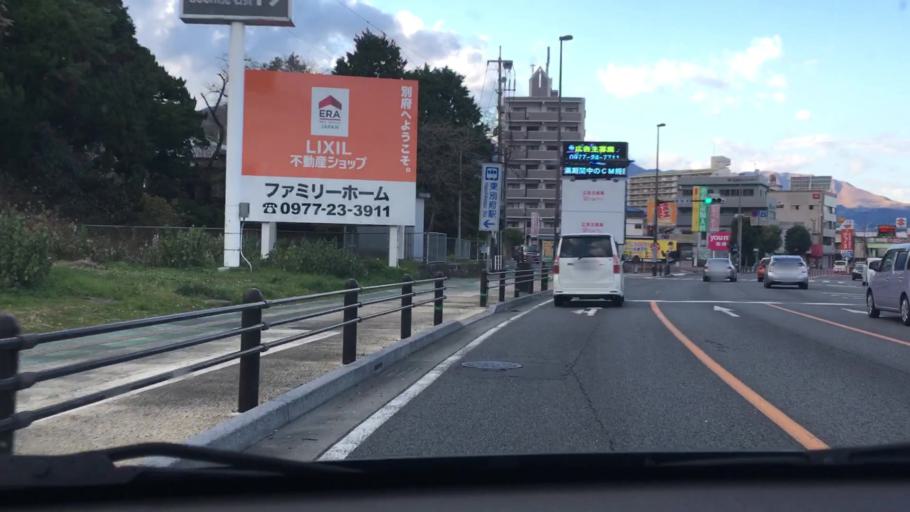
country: JP
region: Oita
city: Beppu
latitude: 33.2677
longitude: 131.5115
